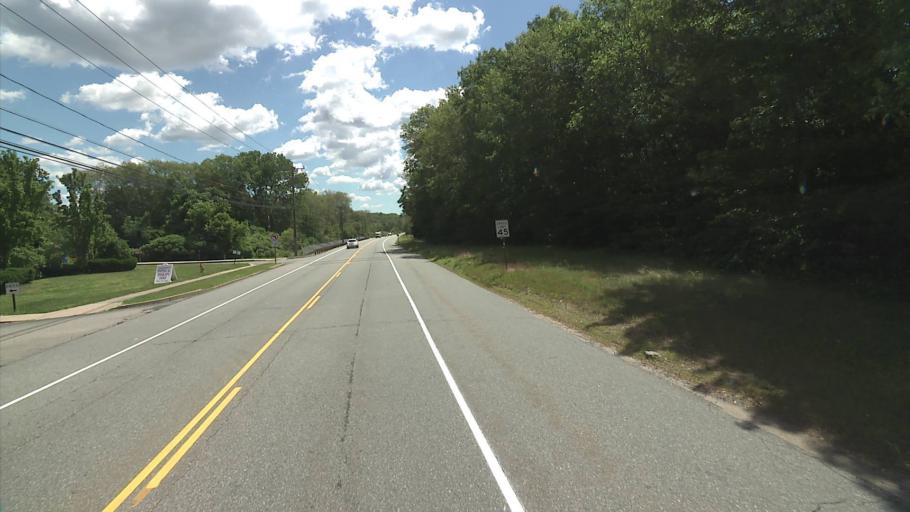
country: US
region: Connecticut
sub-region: New London County
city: Old Mystic
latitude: 41.3897
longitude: -71.9872
